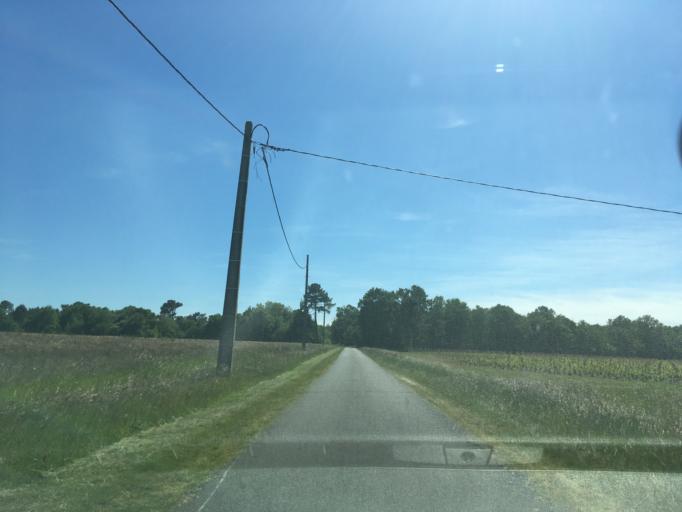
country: FR
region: Aquitaine
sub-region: Departement de la Gironde
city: Lesparre-Medoc
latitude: 45.3047
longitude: -0.8857
